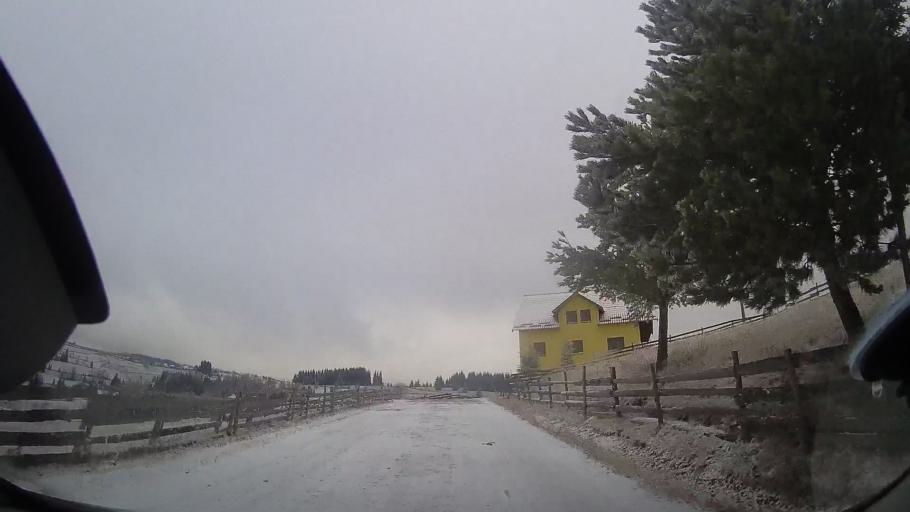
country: RO
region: Cluj
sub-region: Comuna Marisel
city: Marisel
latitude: 46.6590
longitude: 23.1310
